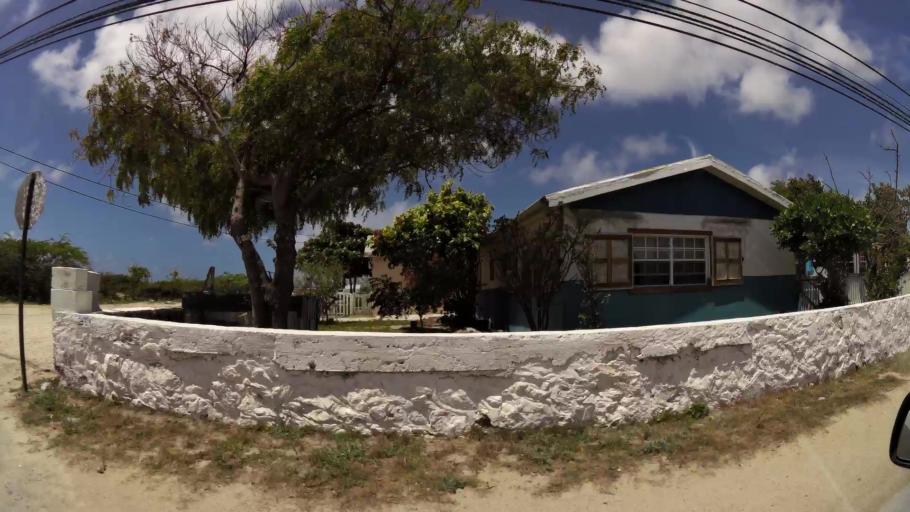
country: TC
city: Cockburn Town
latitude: 21.4606
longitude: -71.1403
